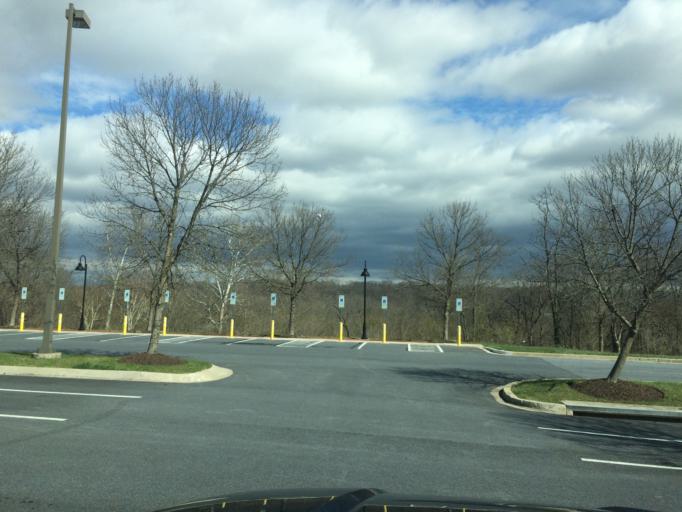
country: US
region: Maryland
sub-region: Frederick County
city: Frederick
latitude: 39.3809
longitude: -77.3955
